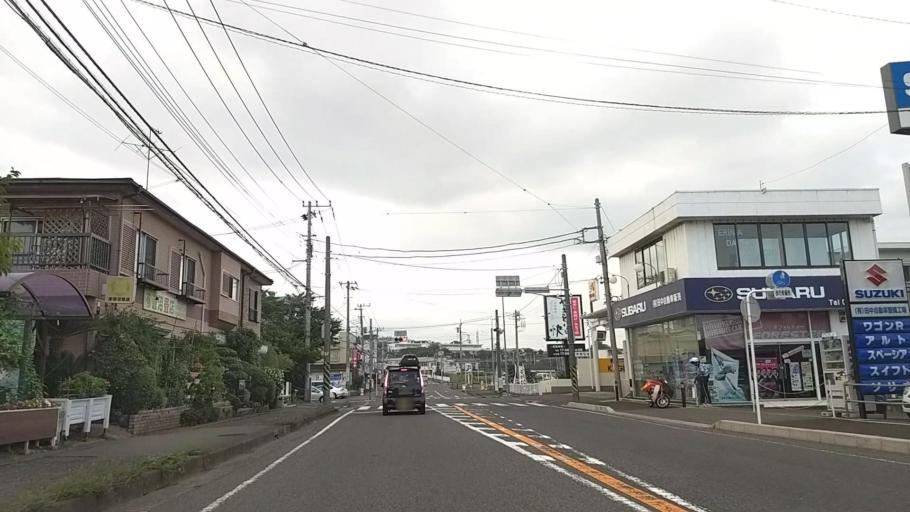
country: JP
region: Kanagawa
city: Isehara
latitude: 35.3845
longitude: 139.3162
